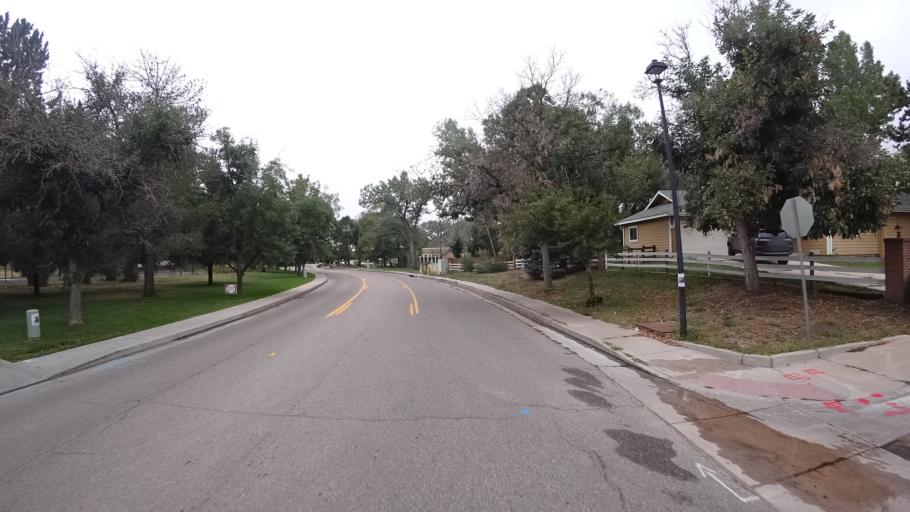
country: US
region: Colorado
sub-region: El Paso County
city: Cimarron Hills
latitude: 38.9311
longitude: -104.7727
